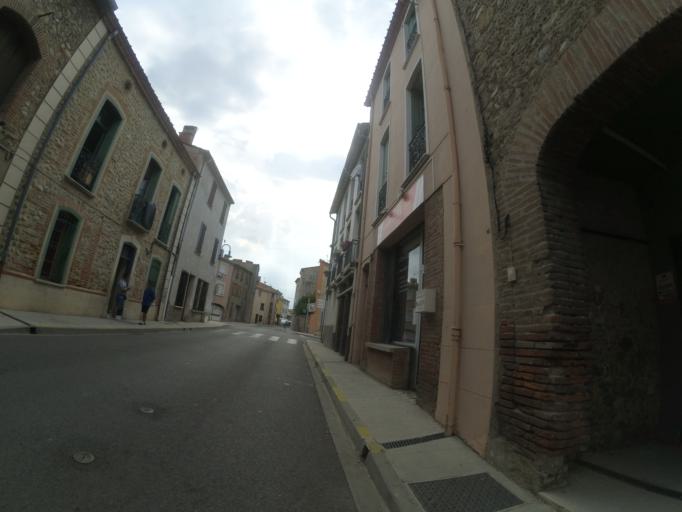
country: FR
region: Languedoc-Roussillon
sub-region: Departement des Pyrenees-Orientales
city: Corneilla-la-Riviere
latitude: 42.6817
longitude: 2.7385
